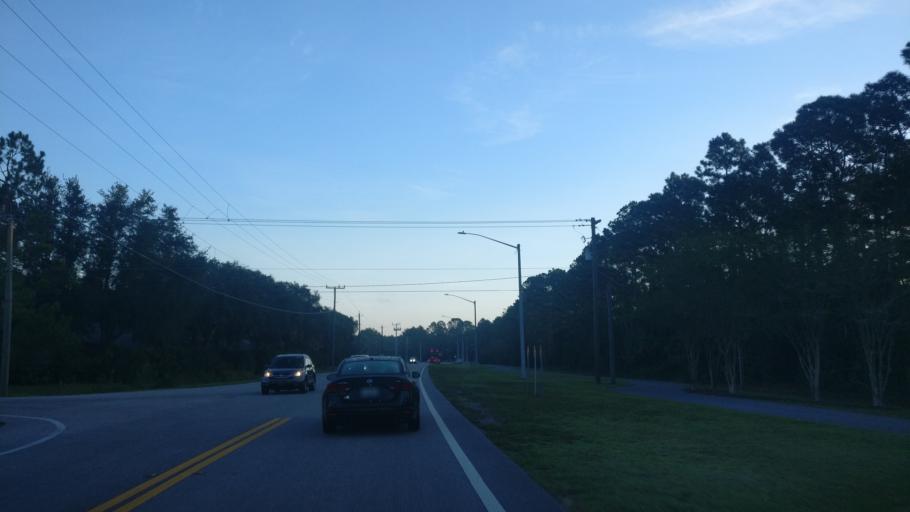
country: US
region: Florida
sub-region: Flagler County
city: Palm Coast
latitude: 29.5434
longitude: -81.2356
